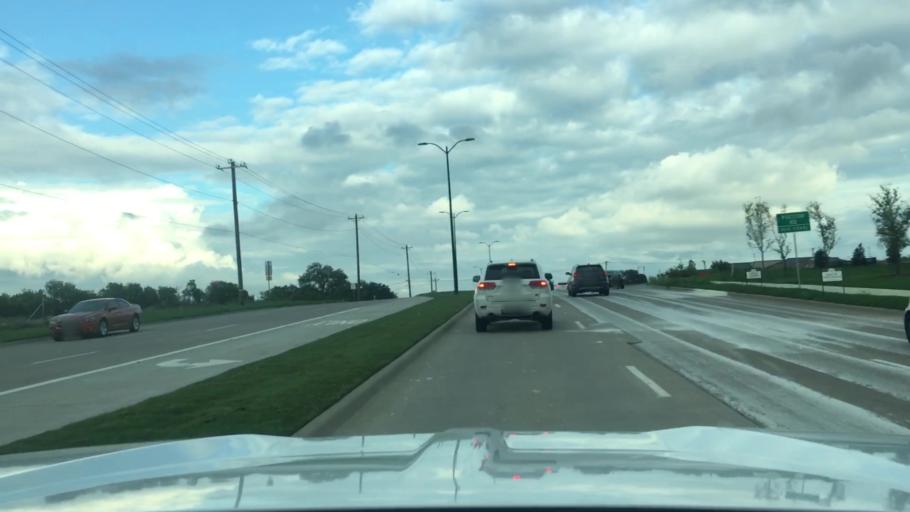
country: US
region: Texas
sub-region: Collin County
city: Frisco
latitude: 33.1746
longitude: -96.8061
